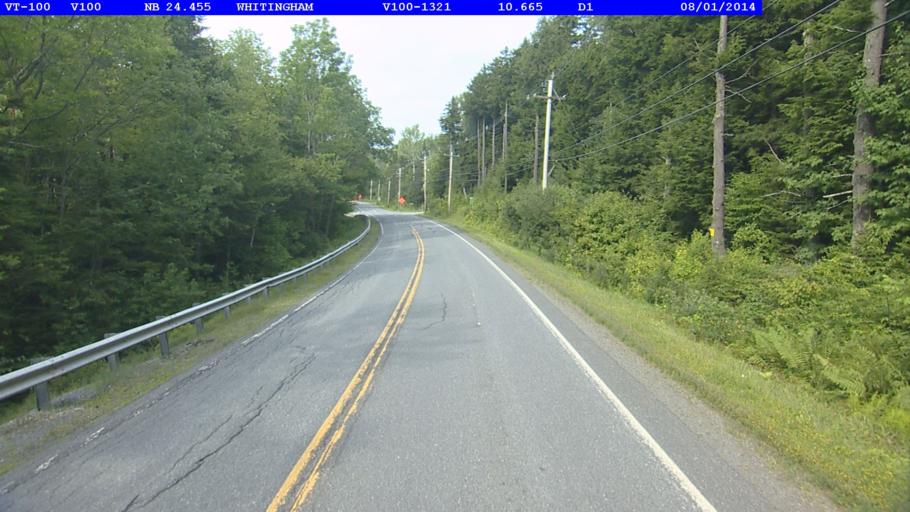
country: US
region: Vermont
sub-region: Windham County
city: Dover
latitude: 42.8272
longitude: -72.8566
